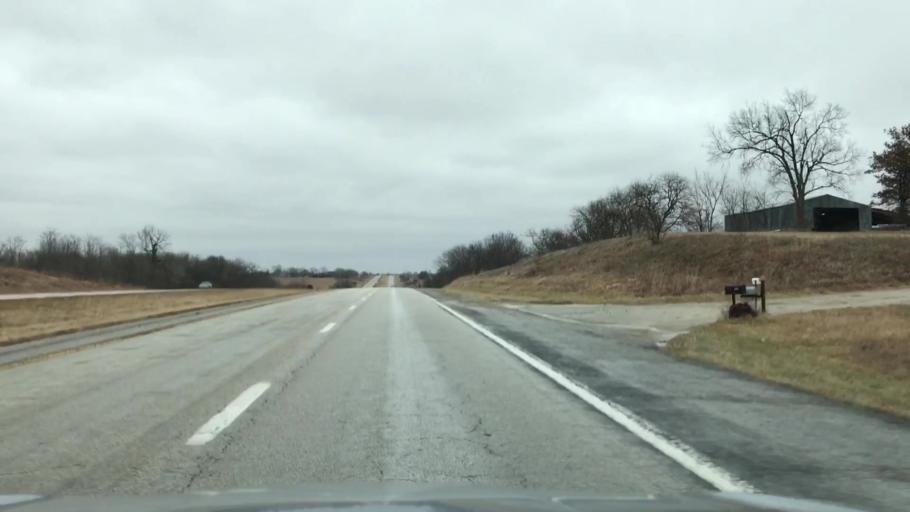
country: US
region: Missouri
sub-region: Caldwell County
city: Hamilton
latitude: 39.7501
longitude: -94.1068
